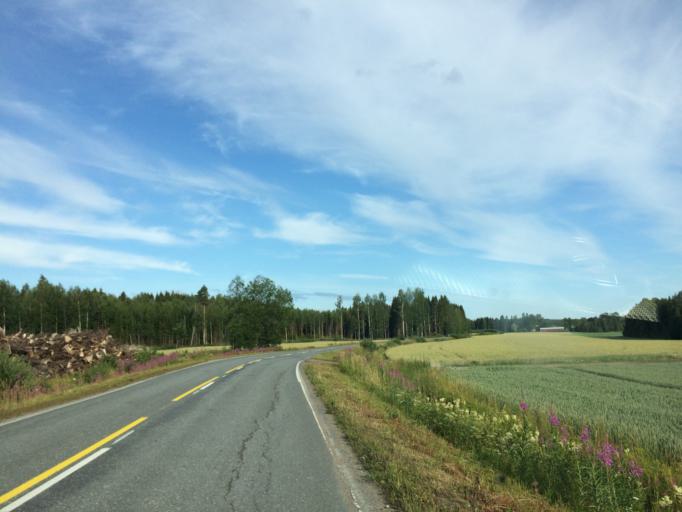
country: FI
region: Haeme
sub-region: Haemeenlinna
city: Janakkala
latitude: 60.9310
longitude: 24.5498
